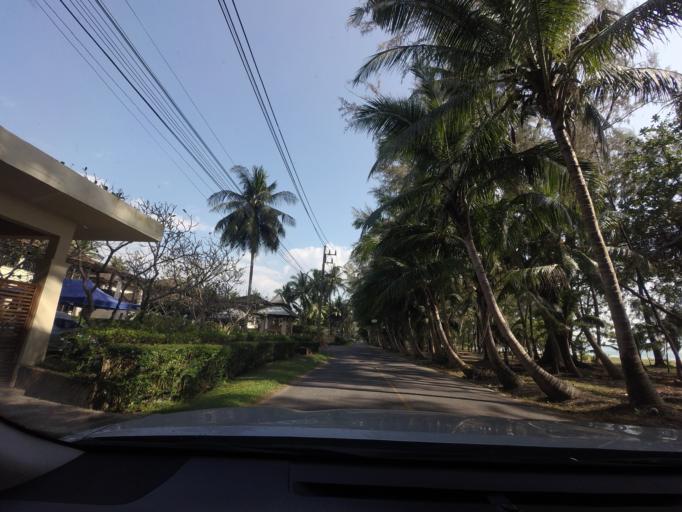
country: TH
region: Phangnga
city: Ban Khao Lak
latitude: 8.7243
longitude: 98.2313
